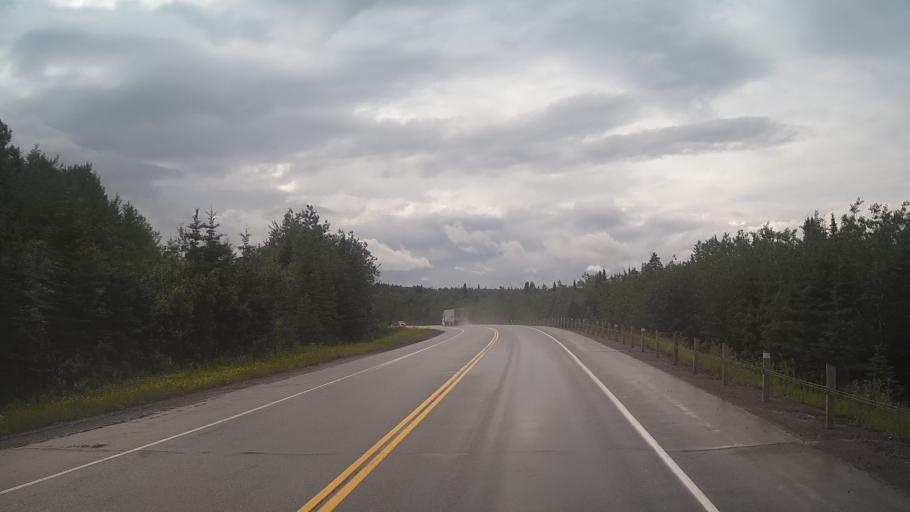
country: CA
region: Ontario
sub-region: Thunder Bay District
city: Thunder Bay
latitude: 48.5442
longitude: -89.6698
